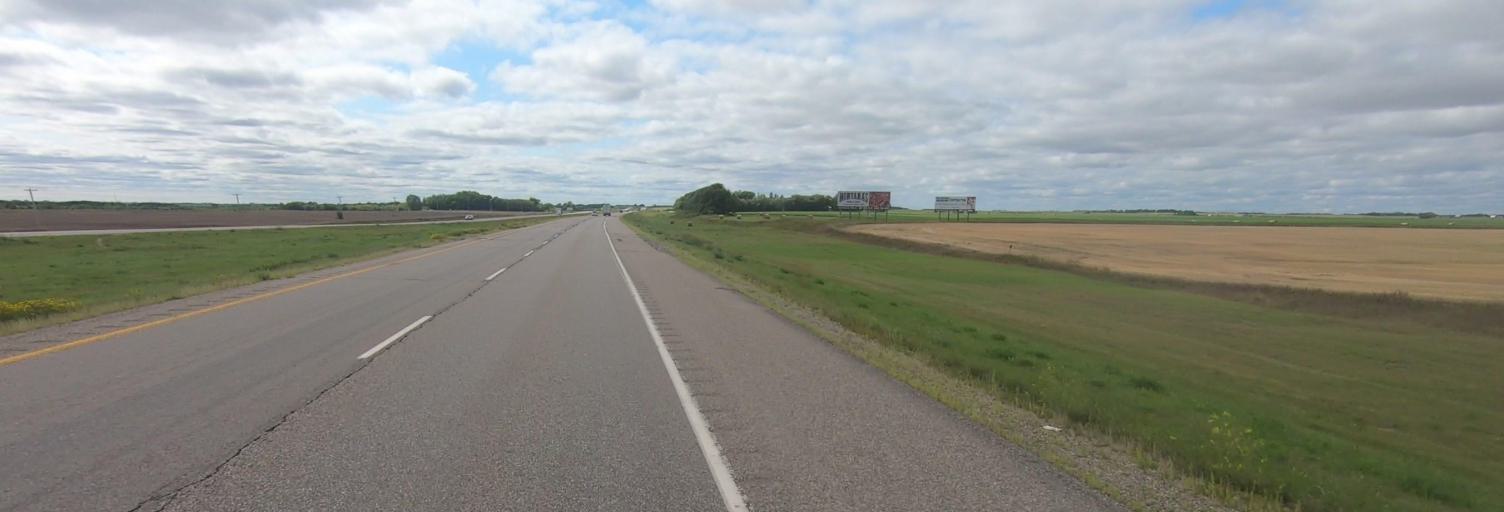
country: CA
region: Manitoba
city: Brandon
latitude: 49.9014
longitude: -99.6695
